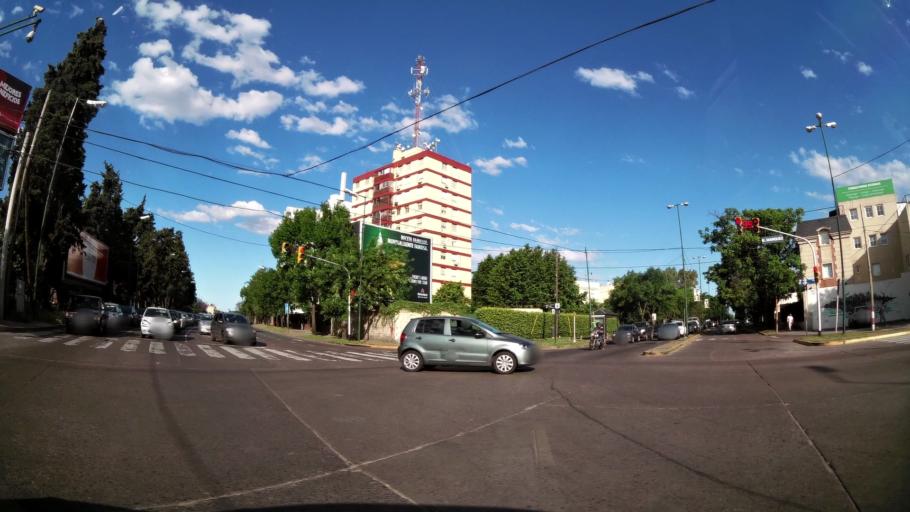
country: AR
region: Buenos Aires
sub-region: Partido de San Isidro
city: San Isidro
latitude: -34.4943
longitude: -58.5512
